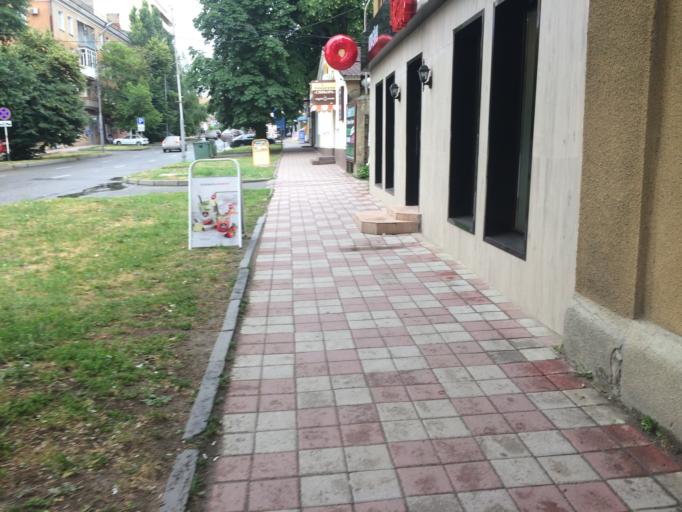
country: RU
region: Stavropol'skiy
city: Stavropol'
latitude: 45.0404
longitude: 41.9628
